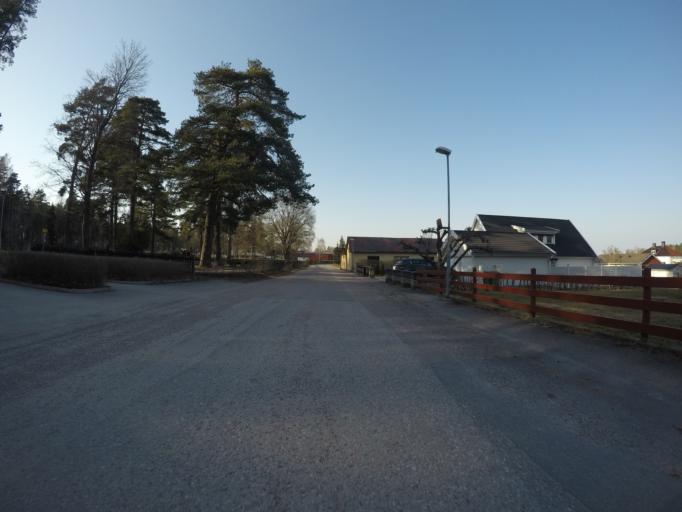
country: SE
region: Vaestmanland
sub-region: Kungsors Kommun
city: Kungsoer
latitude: 59.4165
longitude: 16.1063
